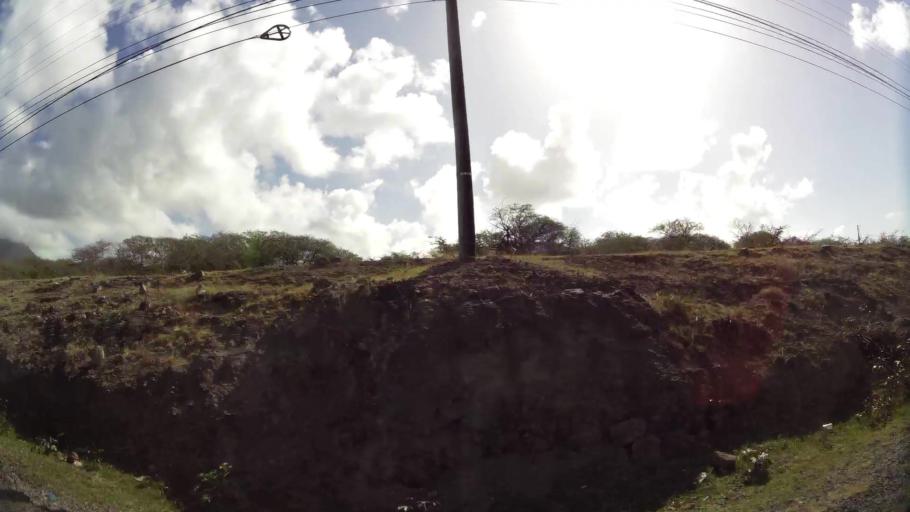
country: KN
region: Saint John Figtree
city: Fig Tree
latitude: 17.1116
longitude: -62.6209
